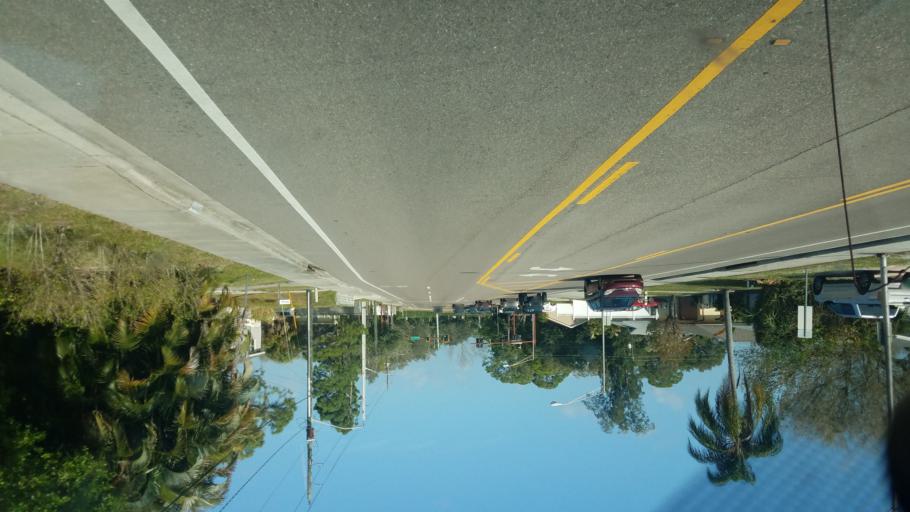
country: US
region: Florida
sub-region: Sarasota County
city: Sarasota Springs
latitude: 27.3141
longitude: -82.4822
